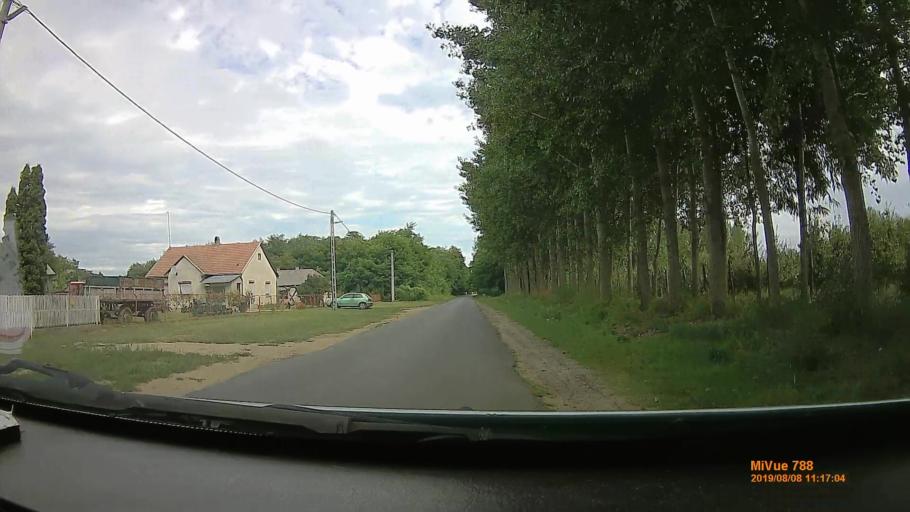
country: HU
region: Szabolcs-Szatmar-Bereg
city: Balkany
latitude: 47.7278
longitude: 21.8306
